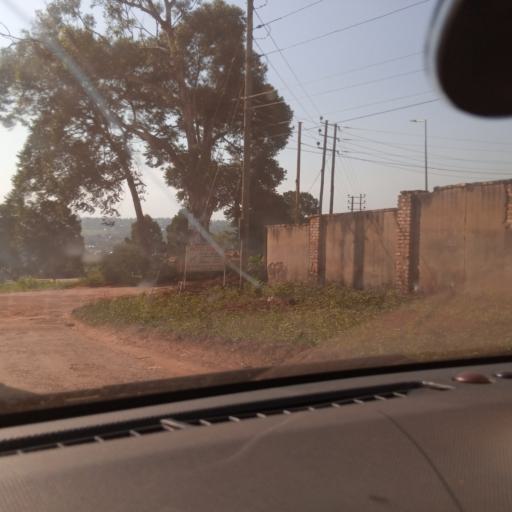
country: UG
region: Central Region
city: Masaka
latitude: -0.3328
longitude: 31.7369
